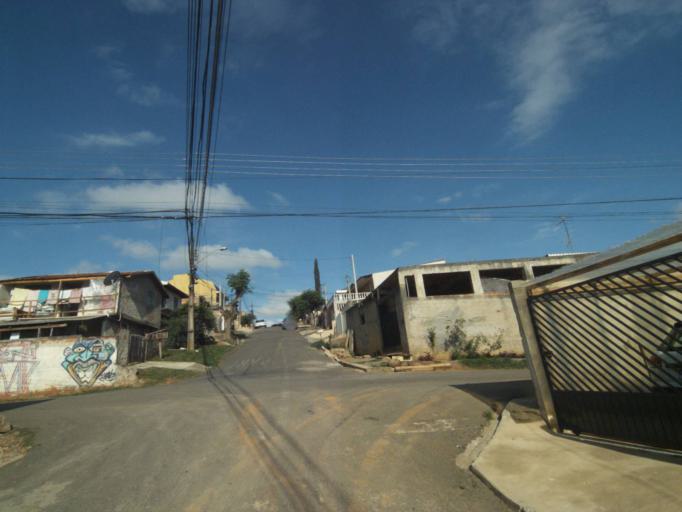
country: BR
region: Parana
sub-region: Curitiba
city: Curitiba
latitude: -25.3934
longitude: -49.3035
